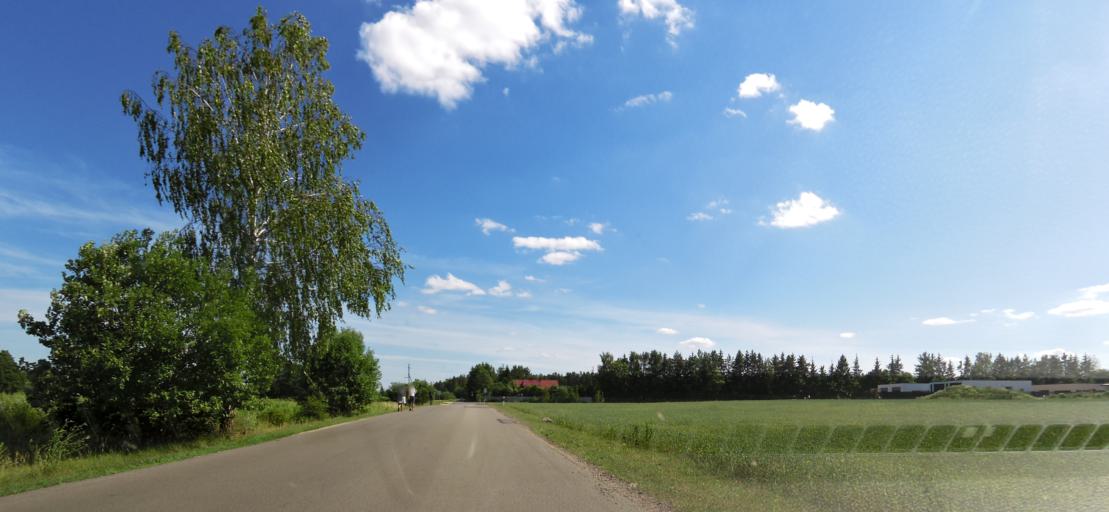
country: LT
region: Vilnius County
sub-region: Vilnius
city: Fabijoniskes
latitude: 54.8077
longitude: 25.3262
